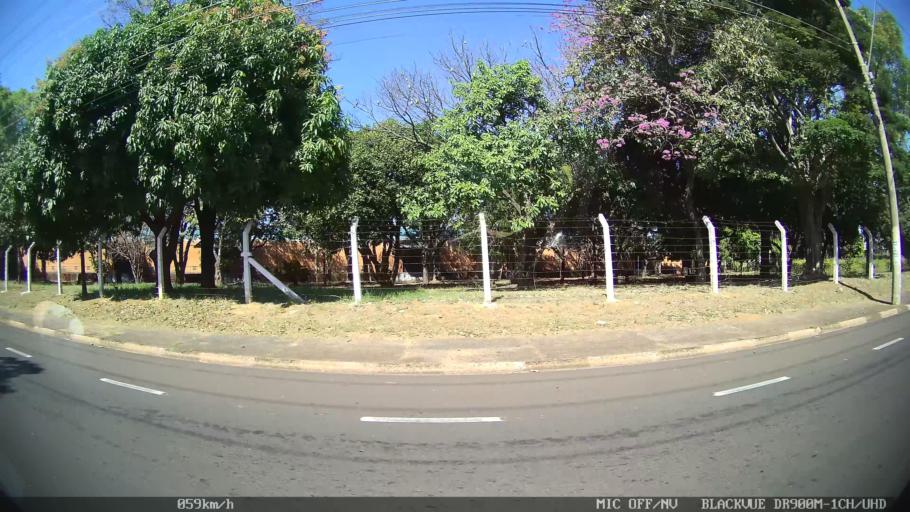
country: BR
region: Sao Paulo
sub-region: Franca
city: Franca
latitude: -20.5441
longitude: -47.4247
